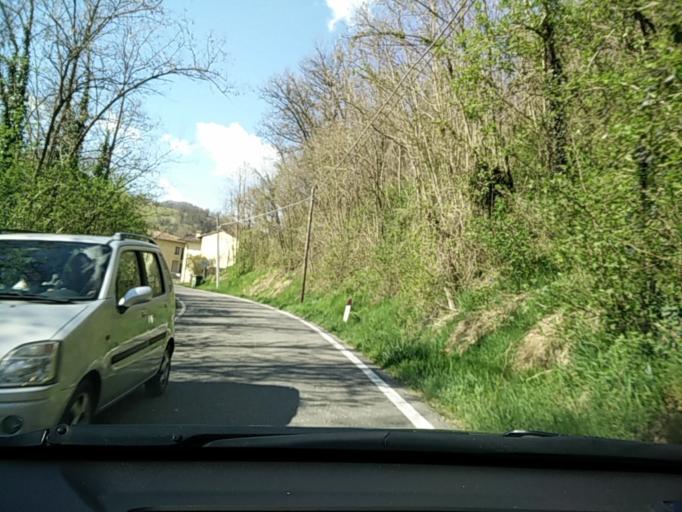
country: IT
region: Lombardy
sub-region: Provincia di Pavia
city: Susella
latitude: 44.8977
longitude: 9.0944
